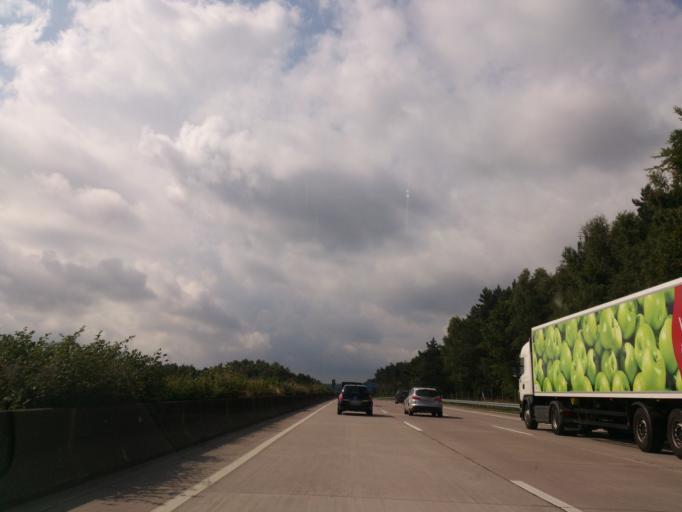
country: DE
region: Lower Saxony
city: Garlstorf
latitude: 53.2461
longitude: 10.0841
